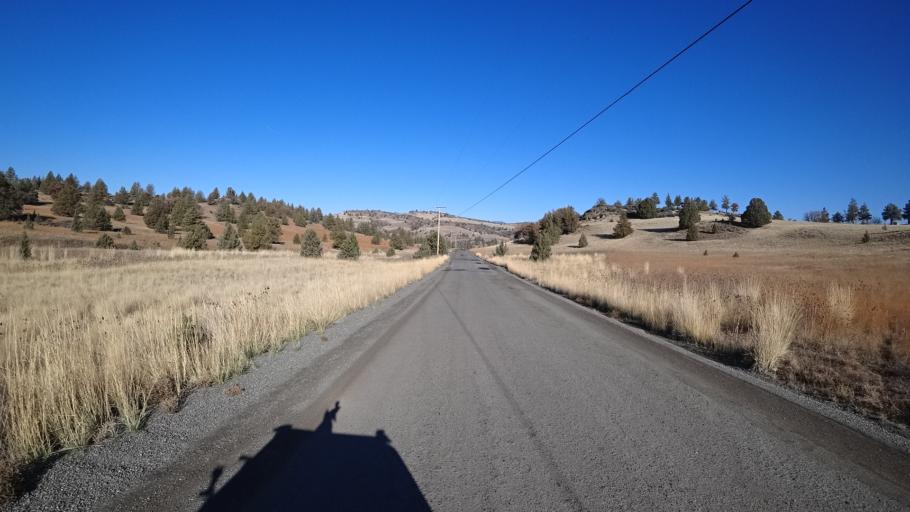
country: US
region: California
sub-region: Siskiyou County
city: Montague
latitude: 41.8839
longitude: -122.4258
